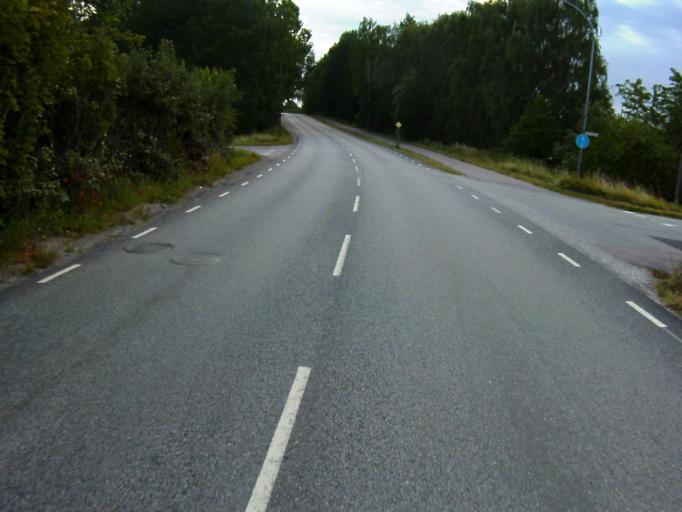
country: SE
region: Soedermanland
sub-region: Eskilstuna Kommun
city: Hallbybrunn
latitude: 59.3757
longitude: 16.4412
